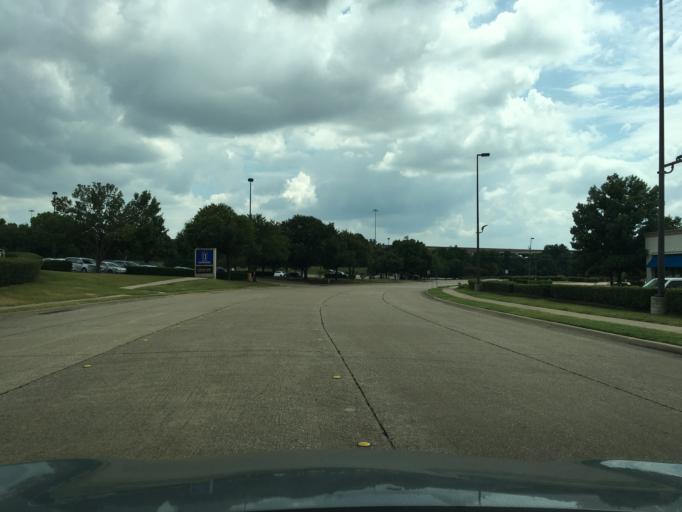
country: US
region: Texas
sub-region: Collin County
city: Plano
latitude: 33.0081
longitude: -96.7102
